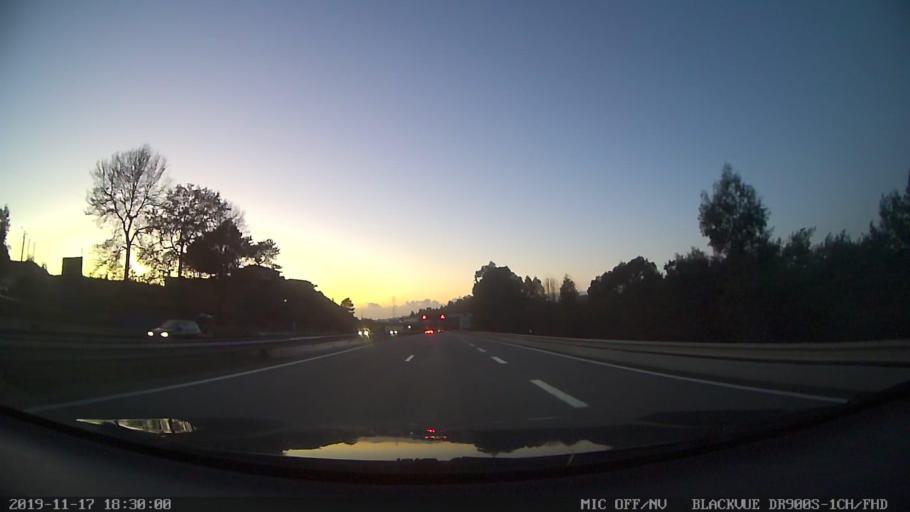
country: PT
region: Porto
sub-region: Valongo
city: Valongo
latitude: 41.2030
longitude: -8.5242
